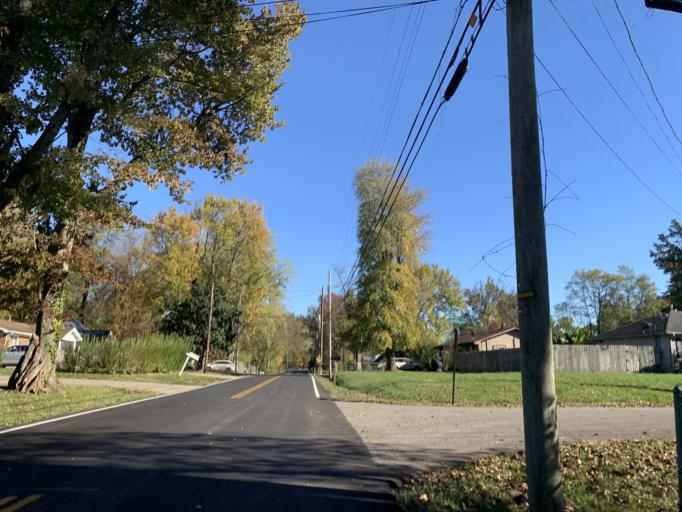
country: US
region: Kentucky
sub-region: Jefferson County
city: Pleasure Ridge Park
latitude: 38.1566
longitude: -85.8724
